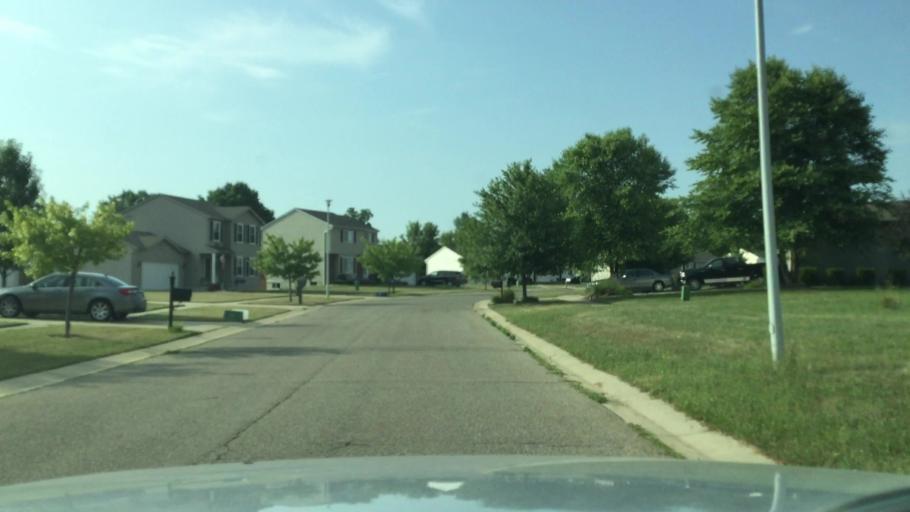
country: US
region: Michigan
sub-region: Genesee County
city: Flushing
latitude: 43.0559
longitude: -83.8649
